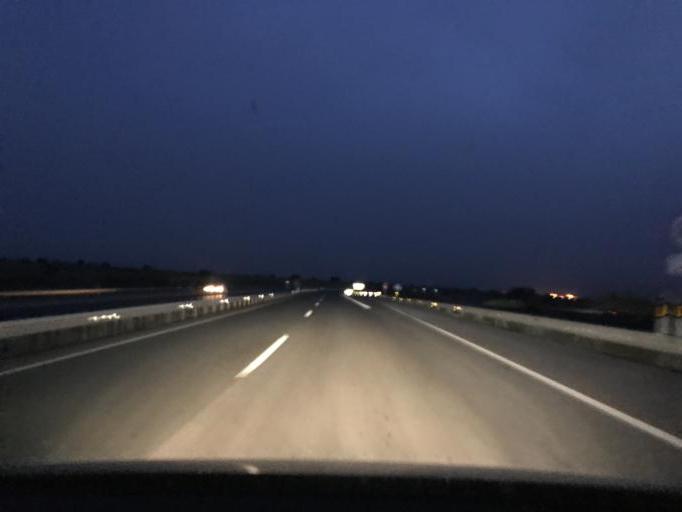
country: ES
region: Andalusia
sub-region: Provincia de Granada
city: Benalua de Guadix
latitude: 37.3717
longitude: -3.0717
